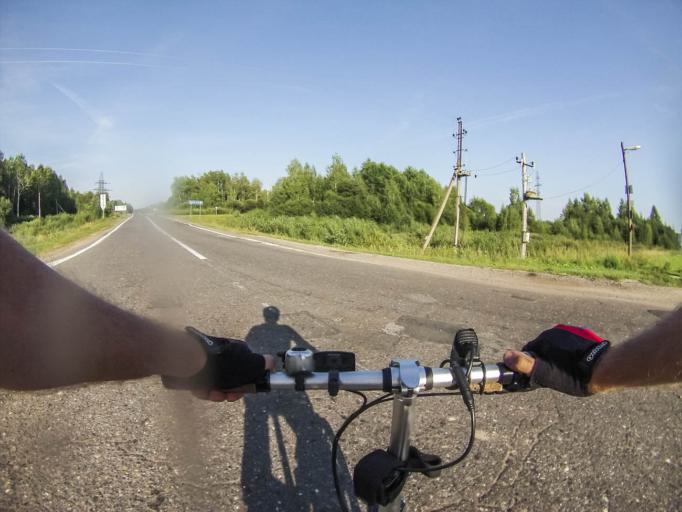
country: RU
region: Jaroslavl
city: Uglich
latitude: 57.6793
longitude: 38.3158
